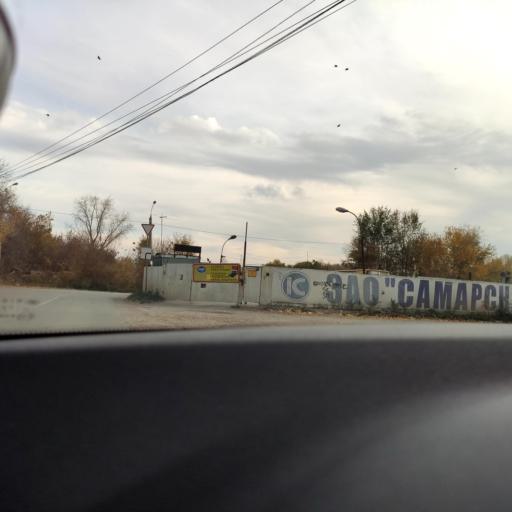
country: RU
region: Samara
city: Smyshlyayevka
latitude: 53.1902
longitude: 50.2777
